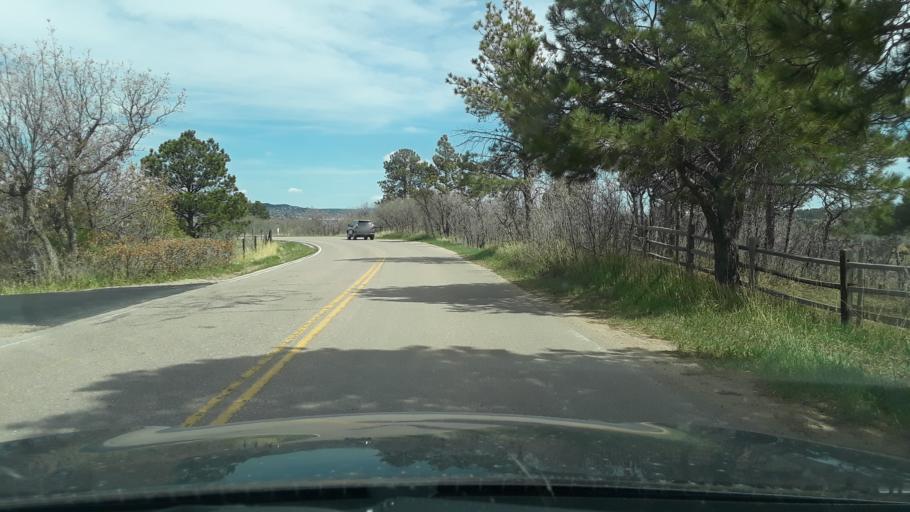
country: US
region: Colorado
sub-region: El Paso County
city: Monument
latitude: 39.0828
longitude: -104.8864
